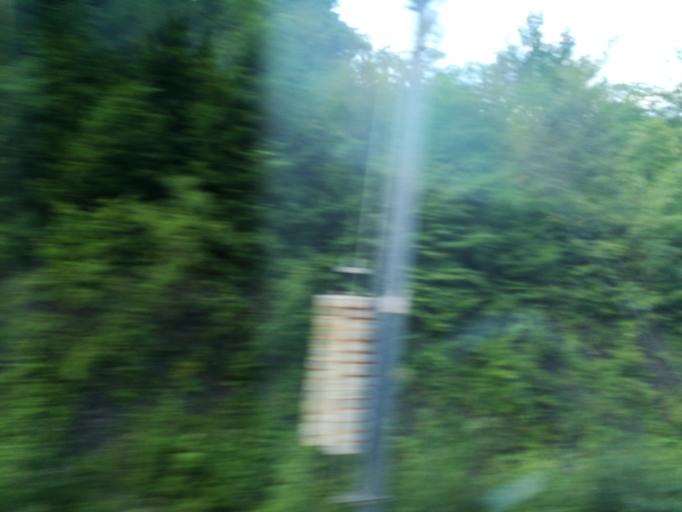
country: RO
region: Prahova
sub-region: Comuna Comarnic
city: Posada
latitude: 45.2882
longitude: 25.6114
